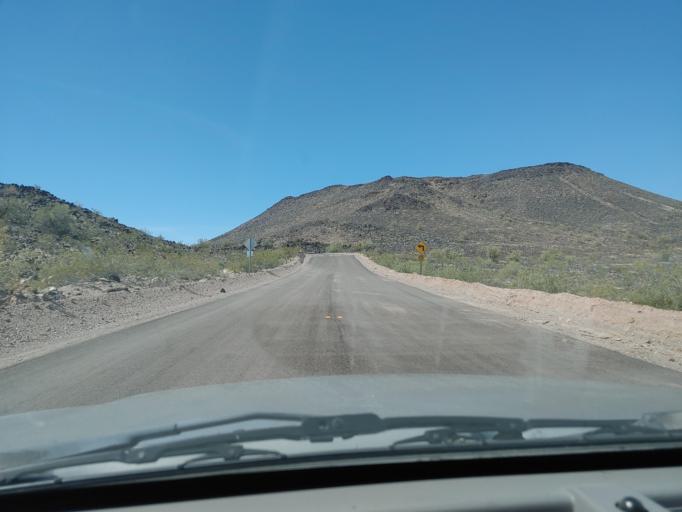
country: US
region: Arizona
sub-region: Maricopa County
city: Gila Bend
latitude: 33.0010
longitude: -113.3408
